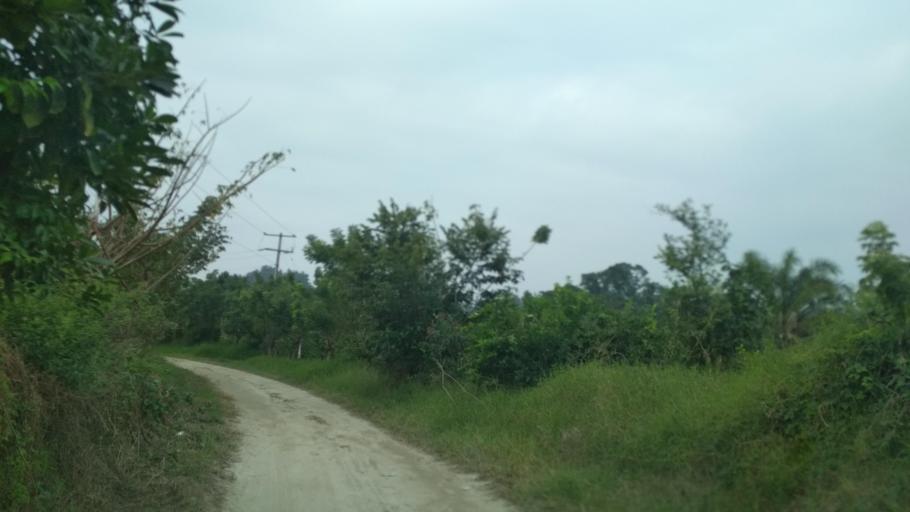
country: MX
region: Puebla
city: Espinal
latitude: 20.2176
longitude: -97.3315
